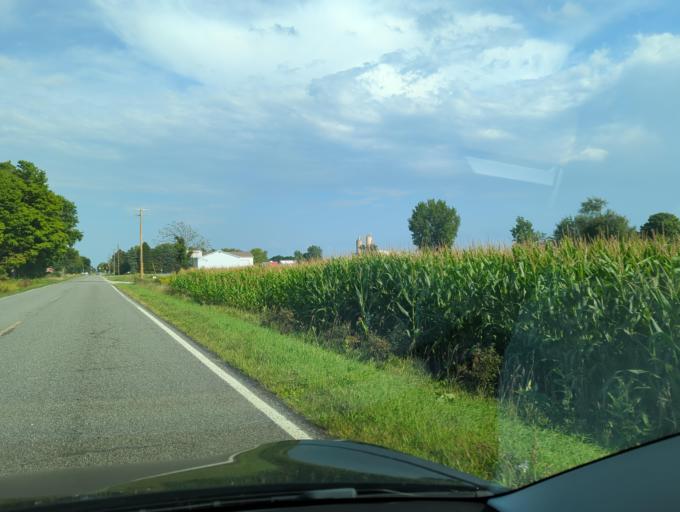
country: US
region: Michigan
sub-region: Ionia County
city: Ionia
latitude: 42.9296
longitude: -85.0811
